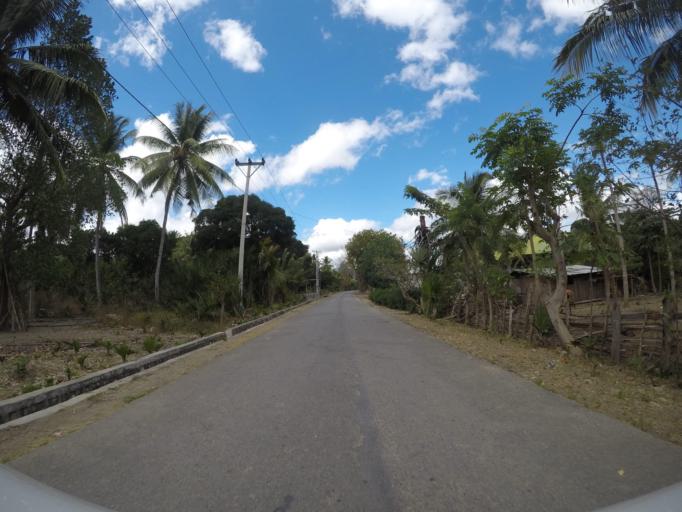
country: TL
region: Lautem
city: Lospalos
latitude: -8.4499
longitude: 126.8235
